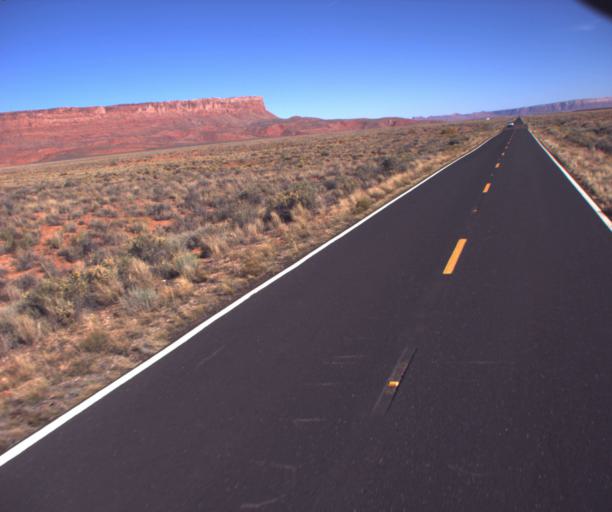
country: US
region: Arizona
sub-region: Coconino County
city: Page
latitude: 36.7014
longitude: -111.9321
